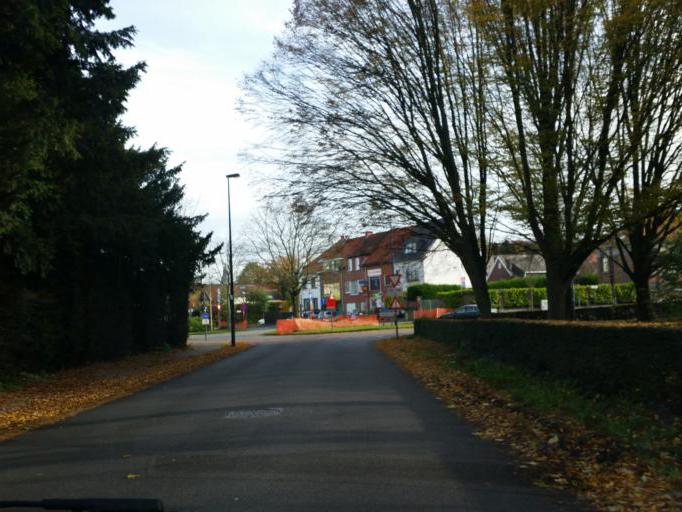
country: BE
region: Flanders
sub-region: Provincie Antwerpen
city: Kontich
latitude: 51.1401
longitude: 4.4453
